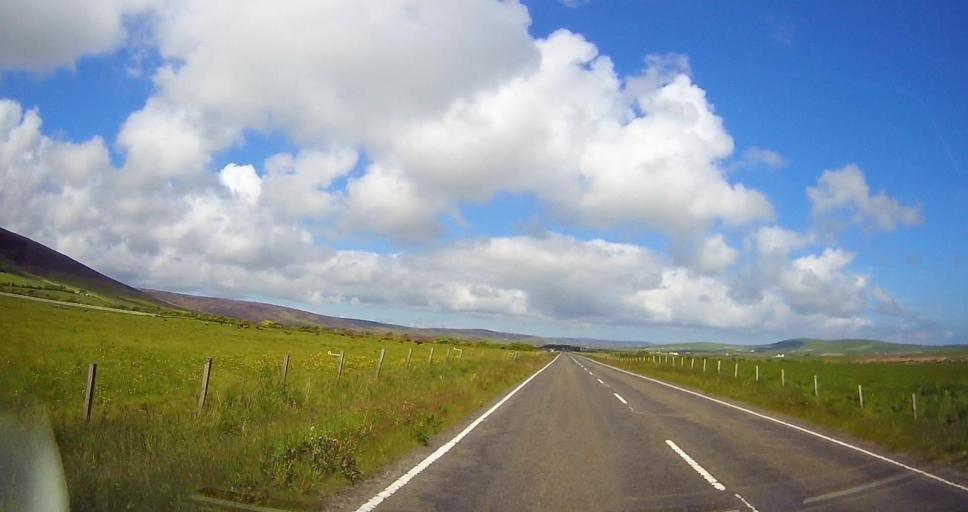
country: GB
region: Scotland
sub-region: Orkney Islands
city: Orkney
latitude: 59.0331
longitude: -3.0911
